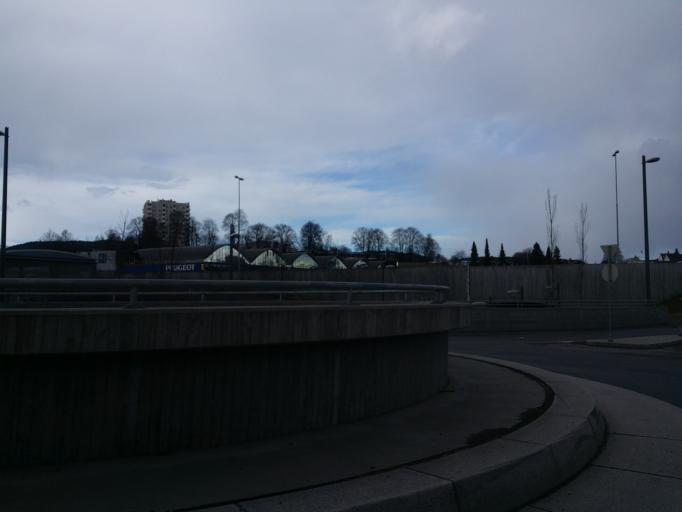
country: NO
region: Oslo
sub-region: Oslo
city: Oslo
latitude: 59.9279
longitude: 10.8077
